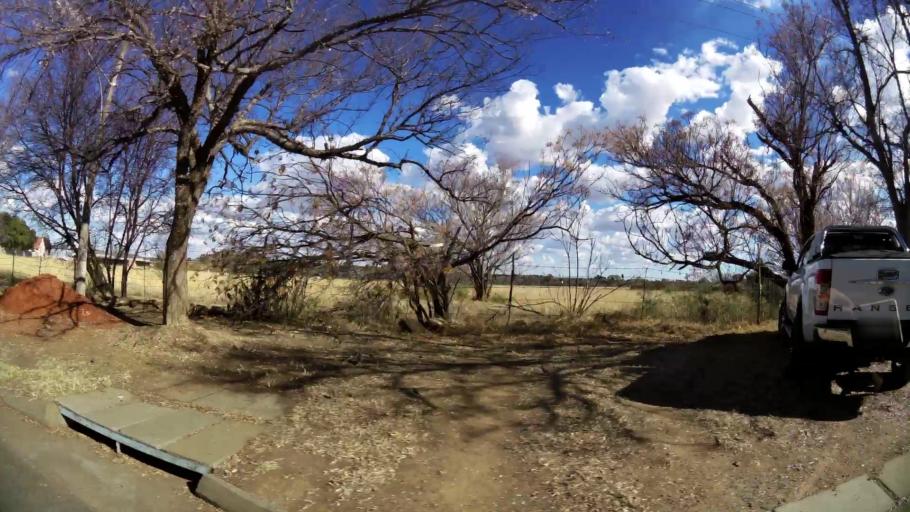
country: ZA
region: North-West
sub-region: Dr Kenneth Kaunda District Municipality
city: Klerksdorp
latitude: -26.8454
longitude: 26.6516
